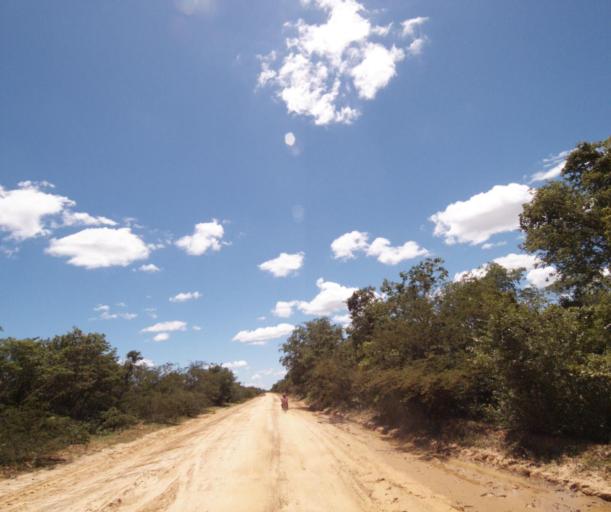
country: BR
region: Bahia
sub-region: Carinhanha
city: Carinhanha
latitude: -14.2052
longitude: -43.9678
